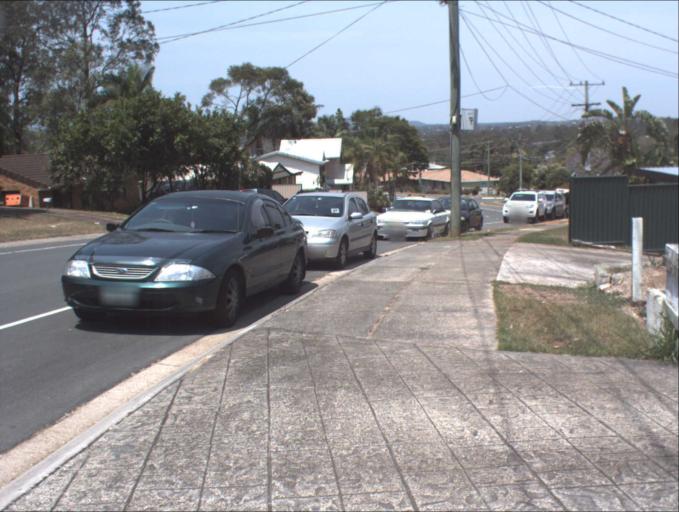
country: AU
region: Queensland
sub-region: Logan
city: Slacks Creek
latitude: -27.6642
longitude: 153.1922
